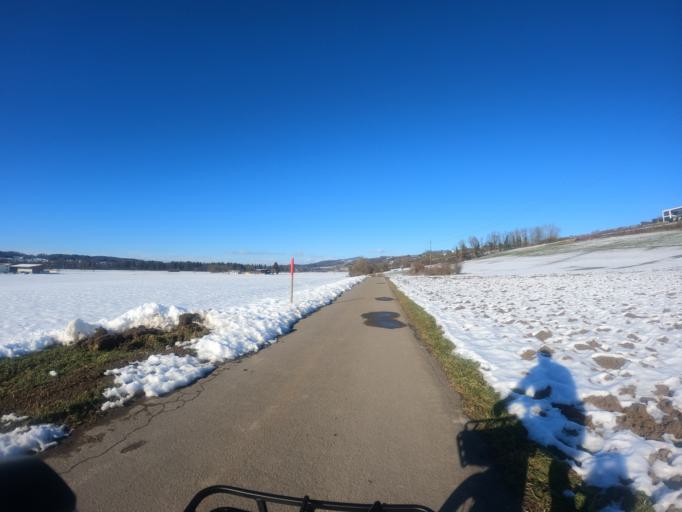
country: CH
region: Aargau
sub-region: Bezirk Bremgarten
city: Jonen
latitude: 47.3015
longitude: 8.3882
